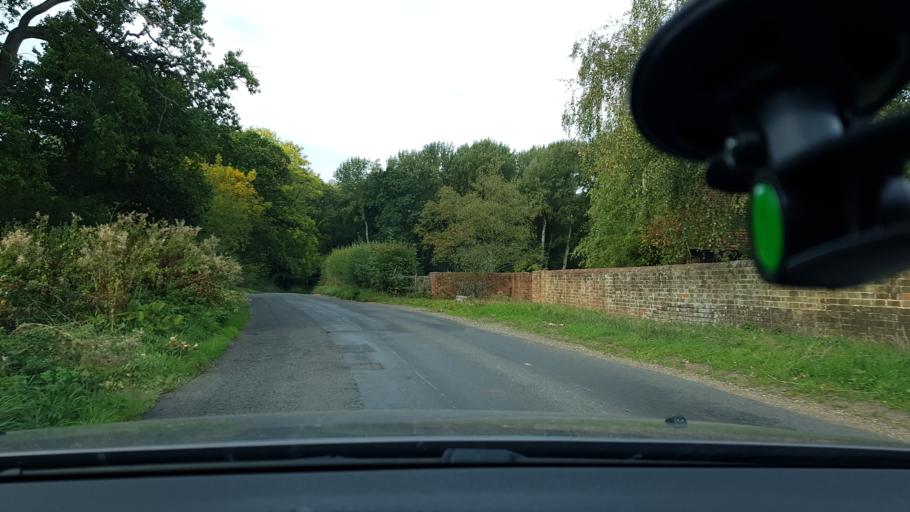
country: GB
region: England
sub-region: West Berkshire
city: Kintbury
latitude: 51.3889
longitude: -1.4219
